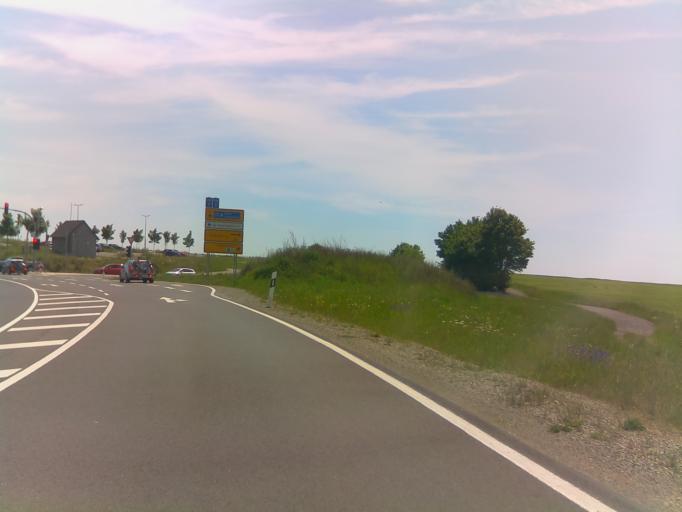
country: DE
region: Bavaria
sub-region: Regierungsbezirk Unterfranken
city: Oerlenbach
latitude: 50.1459
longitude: 10.1496
